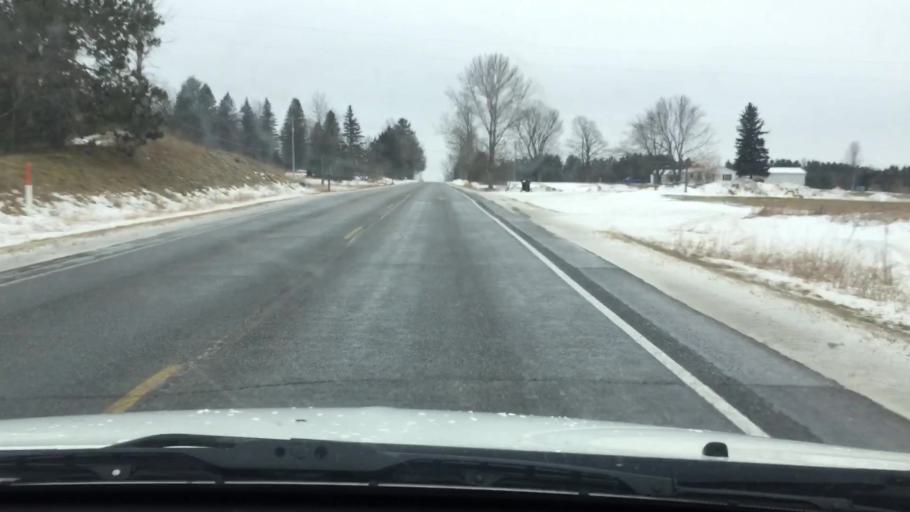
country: US
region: Michigan
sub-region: Wexford County
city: Cadillac
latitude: 44.0702
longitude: -85.4440
